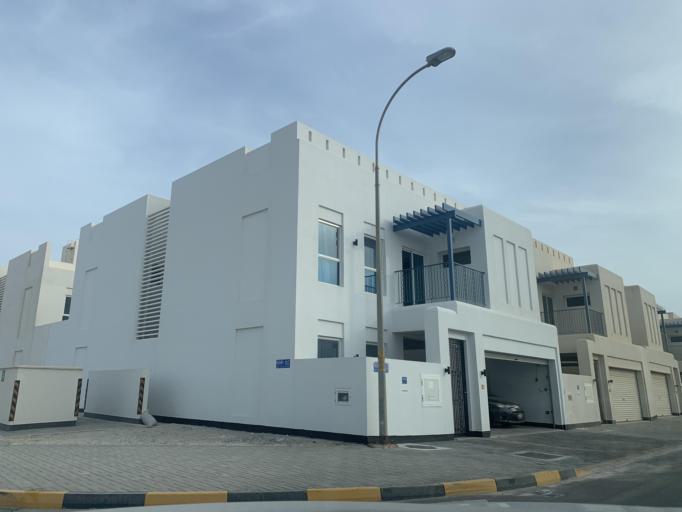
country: BH
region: Muharraq
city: Al Muharraq
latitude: 26.3170
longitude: 50.6219
